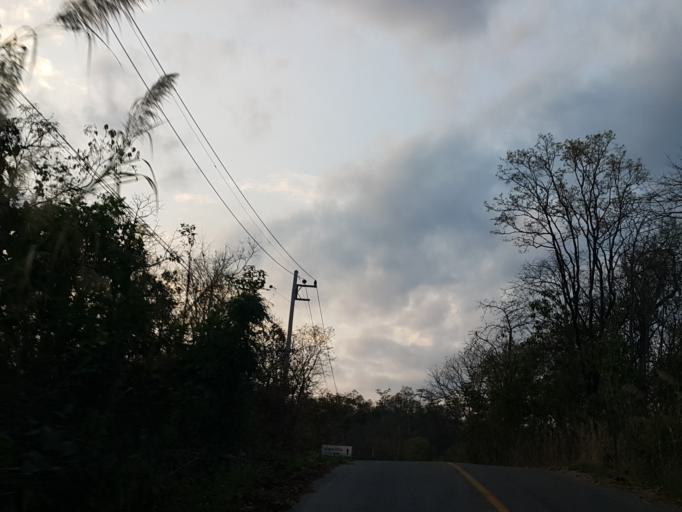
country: TH
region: Lampang
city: Mueang Pan
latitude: 18.8109
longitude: 99.4775
